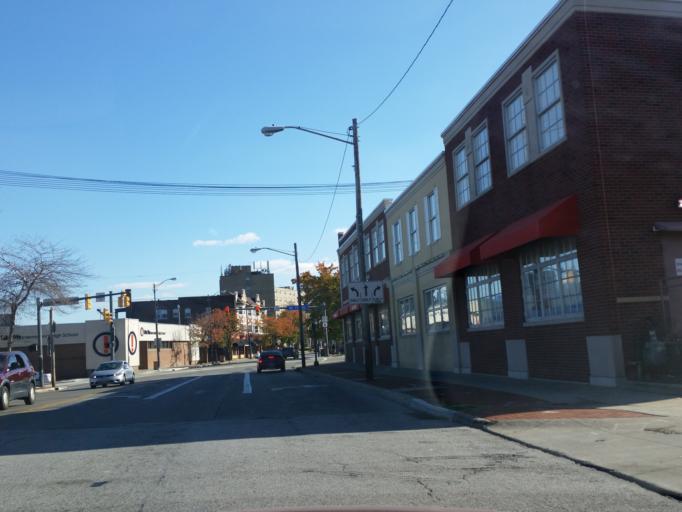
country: US
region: Ohio
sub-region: Cuyahoga County
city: Lakewood
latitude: 41.4837
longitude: -81.7695
